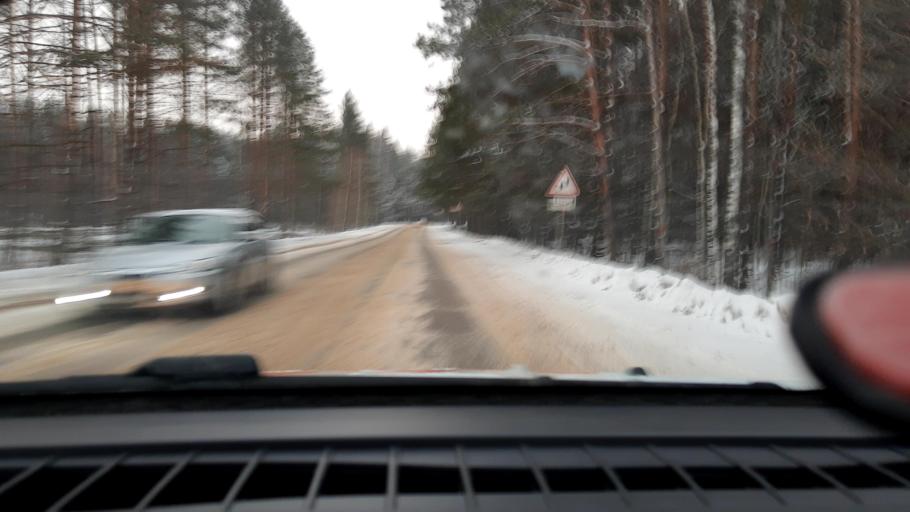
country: RU
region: Nizjnij Novgorod
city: Pamyat' Parizhskoy Kommuny
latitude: 56.2773
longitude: 44.3917
